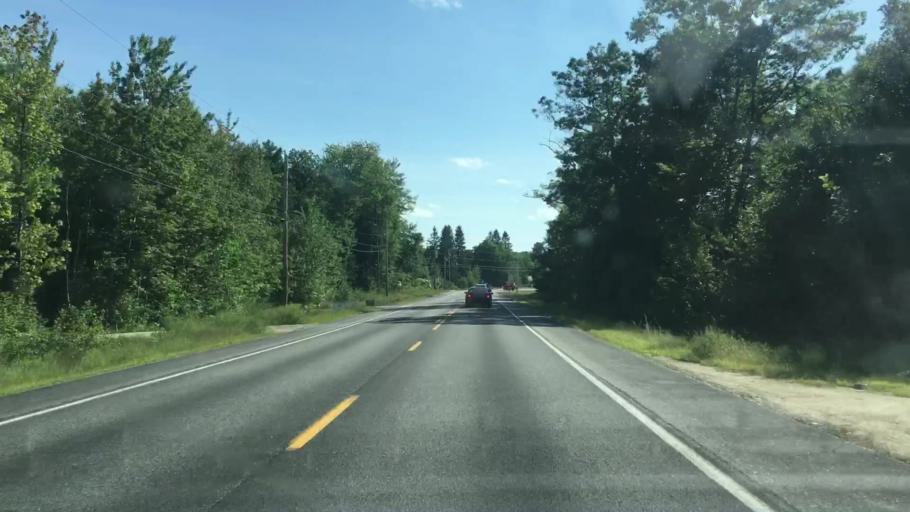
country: US
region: Maine
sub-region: Androscoggin County
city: Lisbon Falls
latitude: 44.0188
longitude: -70.0674
